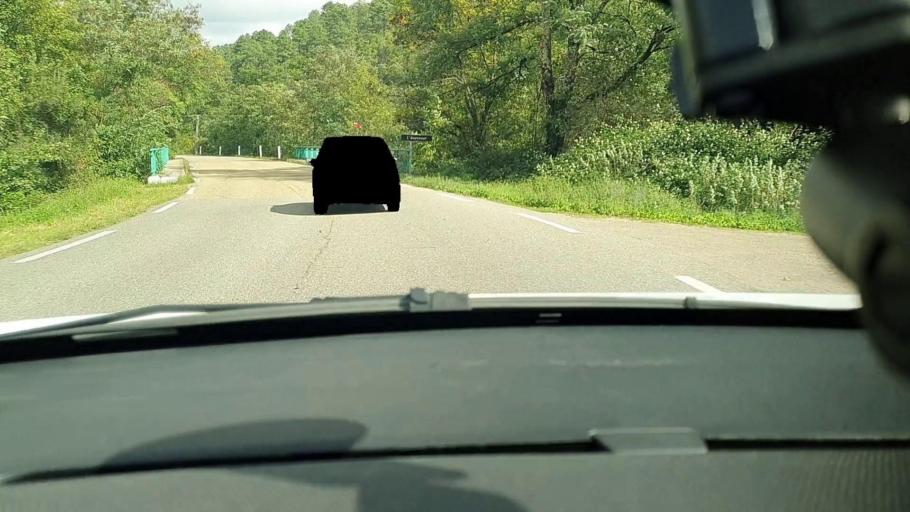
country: FR
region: Languedoc-Roussillon
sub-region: Departement du Gard
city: Laval-Pradel
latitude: 44.2467
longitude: 4.0577
